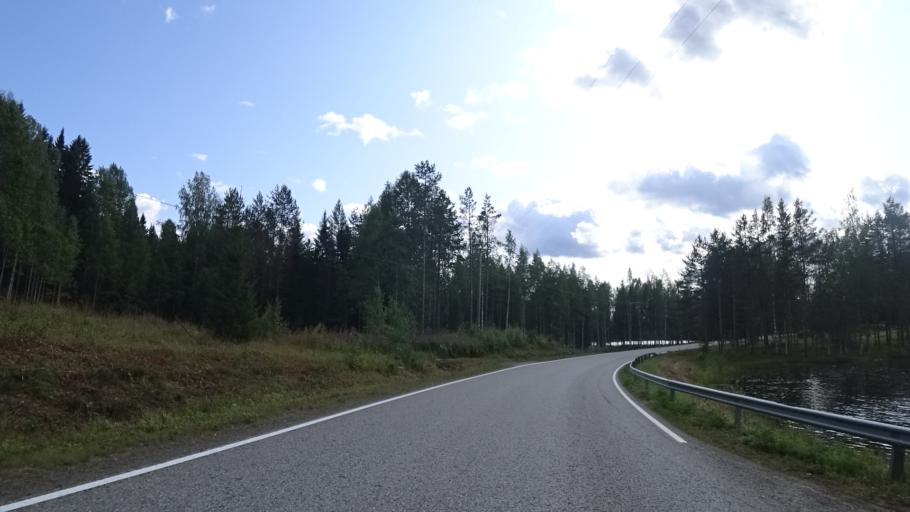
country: RU
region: Republic of Karelia
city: Vyartsilya
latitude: 62.2583
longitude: 30.7649
